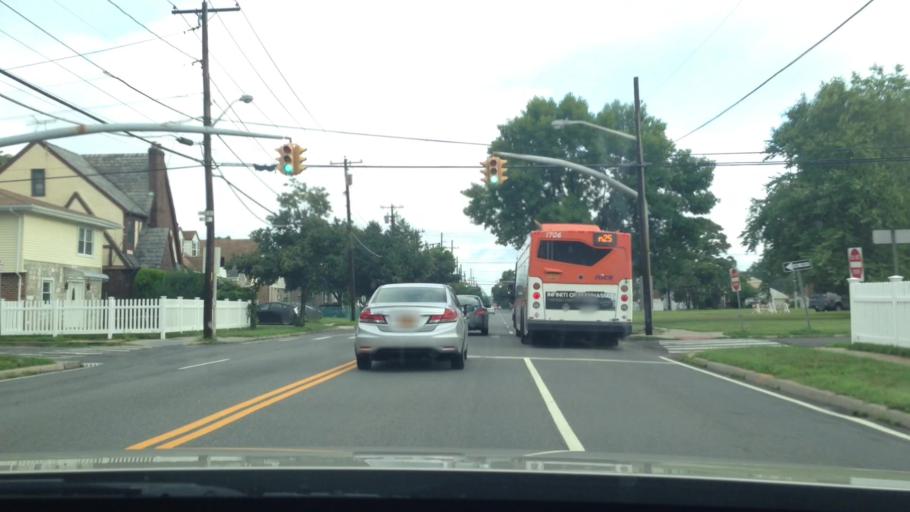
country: US
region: New York
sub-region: Nassau County
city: New Hyde Park
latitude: 40.7348
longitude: -73.6805
